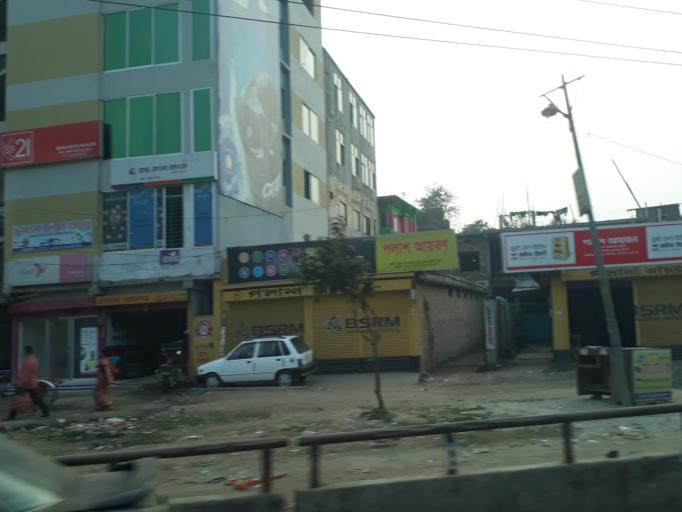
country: BD
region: Khulna
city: Bhatpara Abhaynagar
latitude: 22.9745
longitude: 89.4744
